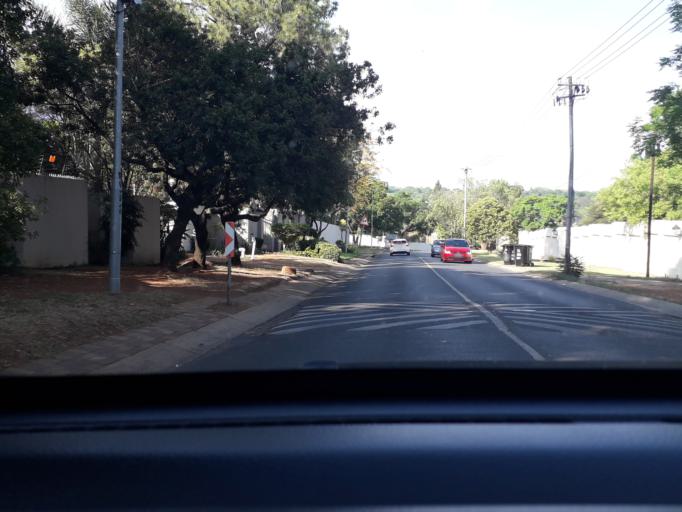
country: ZA
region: Gauteng
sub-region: City of Johannesburg Metropolitan Municipality
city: Midrand
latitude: -26.0684
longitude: 28.0547
